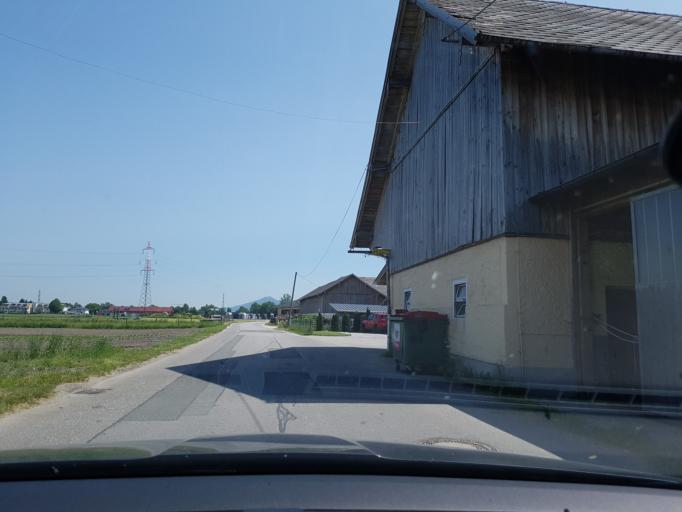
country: DE
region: Bavaria
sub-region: Upper Bavaria
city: Ainring
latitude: 47.7767
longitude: 12.9739
